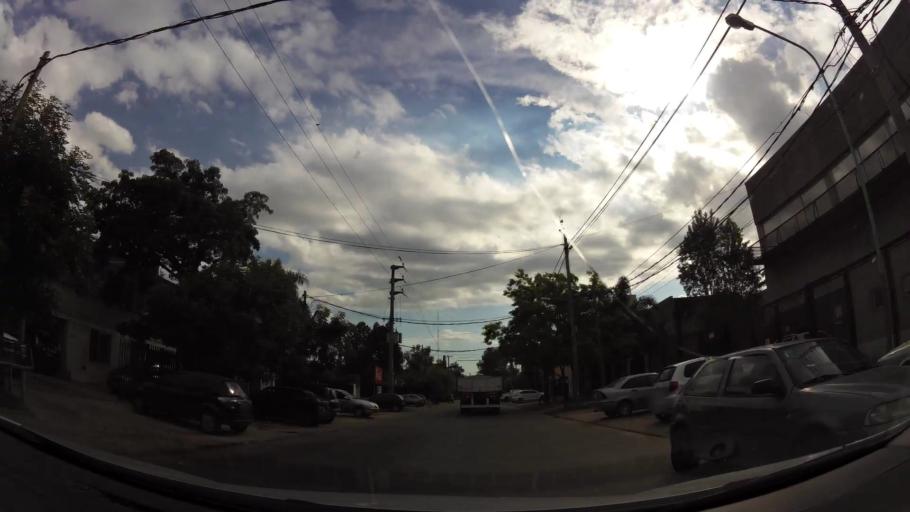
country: AR
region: Buenos Aires
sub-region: Partido de Tigre
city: Tigre
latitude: -34.4798
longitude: -58.6314
